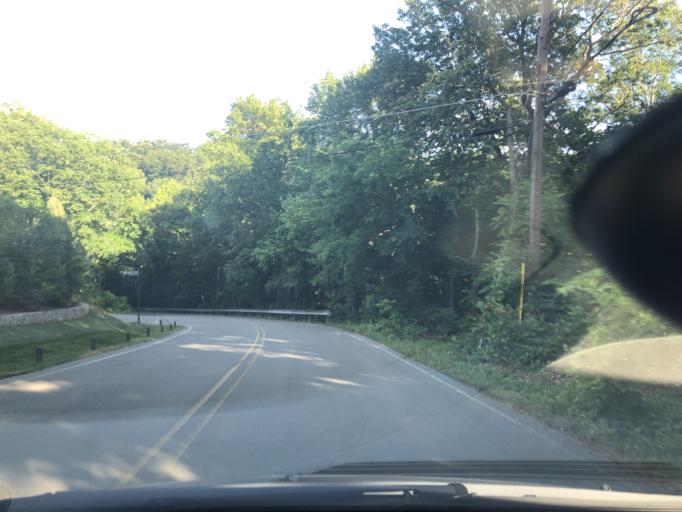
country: US
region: Tennessee
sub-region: Davidson County
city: Forest Hills
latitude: 36.0748
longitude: -86.8189
